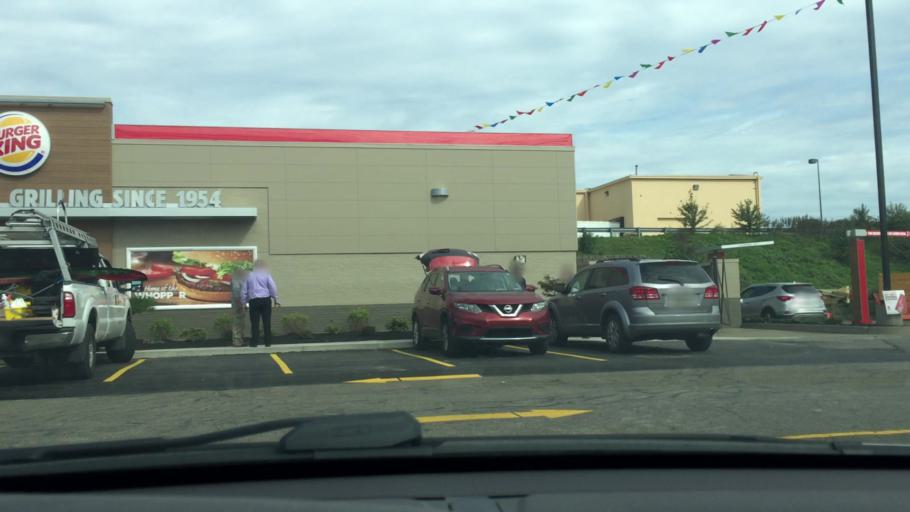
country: US
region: Pennsylvania
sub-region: Allegheny County
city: Enlow
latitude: 40.4501
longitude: -80.1823
